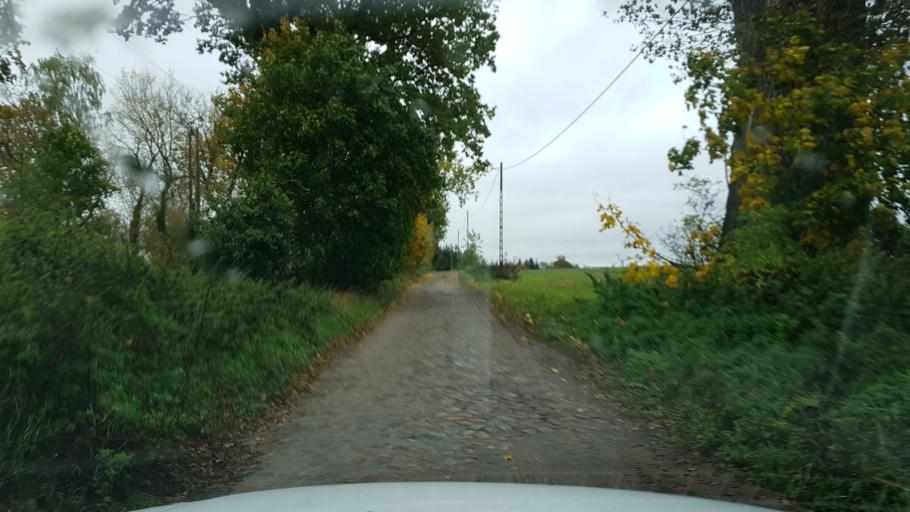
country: PL
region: West Pomeranian Voivodeship
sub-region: Powiat pyrzycki
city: Lipiany
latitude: 52.9696
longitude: 15.0108
